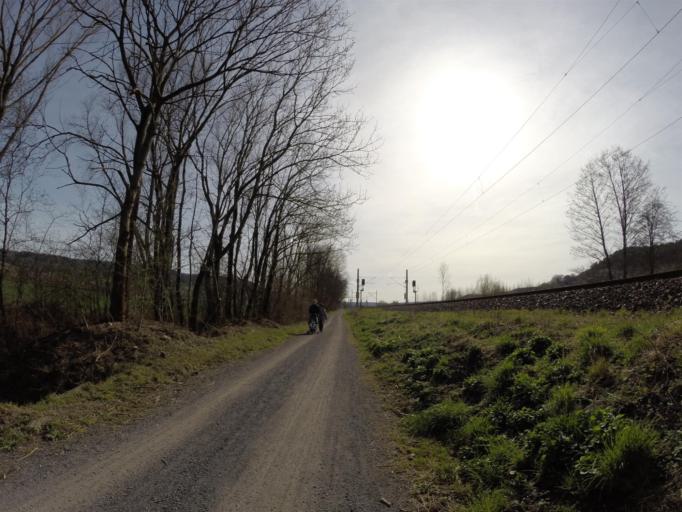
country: DE
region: Thuringia
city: Neuengonna
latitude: 50.9651
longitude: 11.6294
